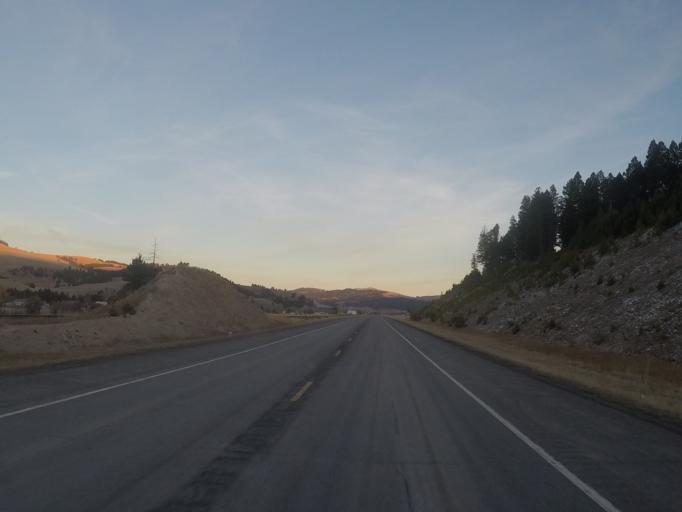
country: US
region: Montana
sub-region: Powell County
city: Deer Lodge
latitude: 46.5652
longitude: -112.4487
